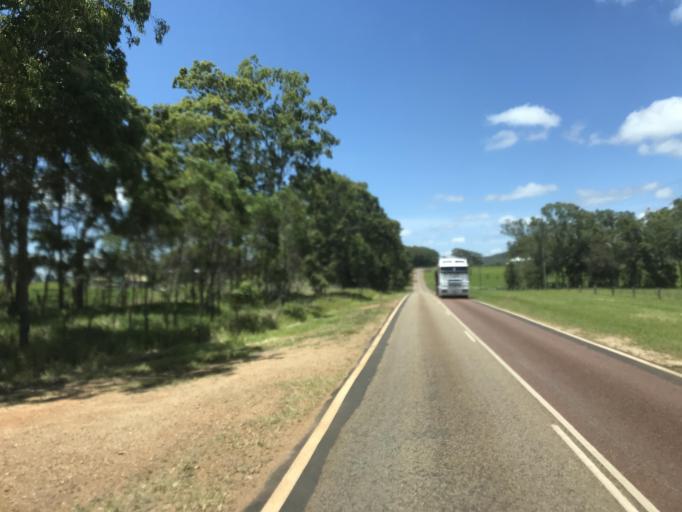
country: AU
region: Queensland
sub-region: Tablelands
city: Ravenshoe
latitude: -17.5194
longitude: 145.4517
